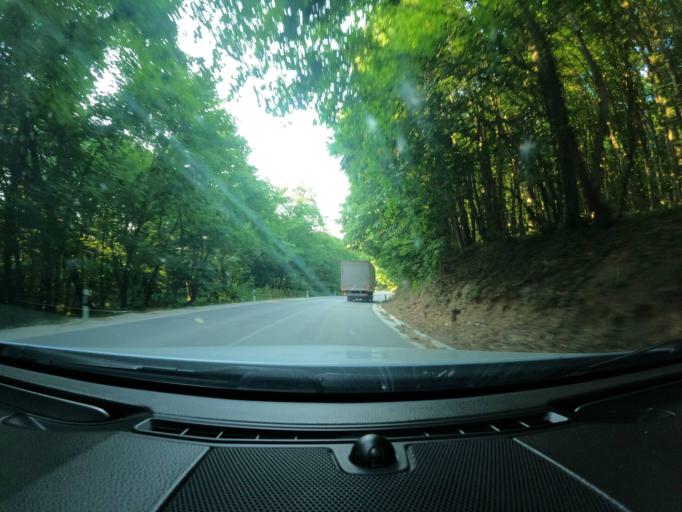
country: RS
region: Autonomna Pokrajina Vojvodina
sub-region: Juznobacki Okrug
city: Beocin
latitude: 45.1538
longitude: 19.7153
